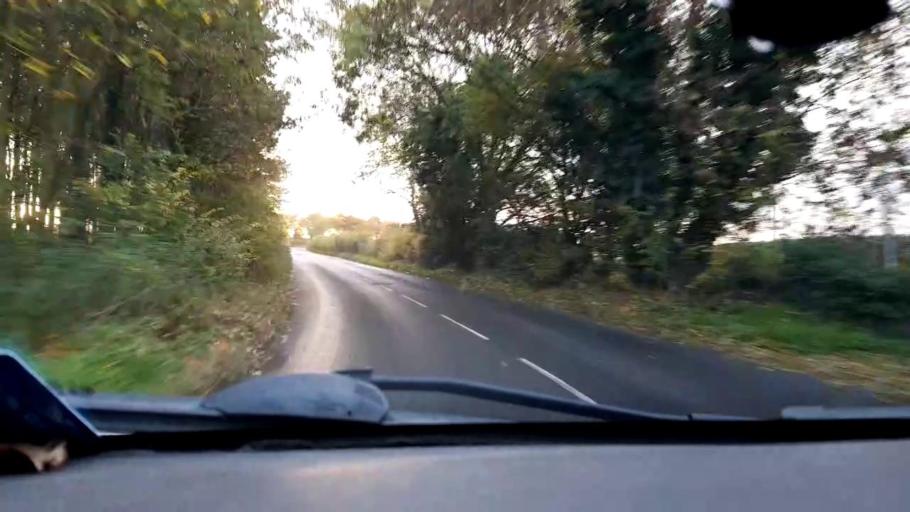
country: GB
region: England
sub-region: Norfolk
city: Spixworth
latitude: 52.6913
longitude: 1.3063
